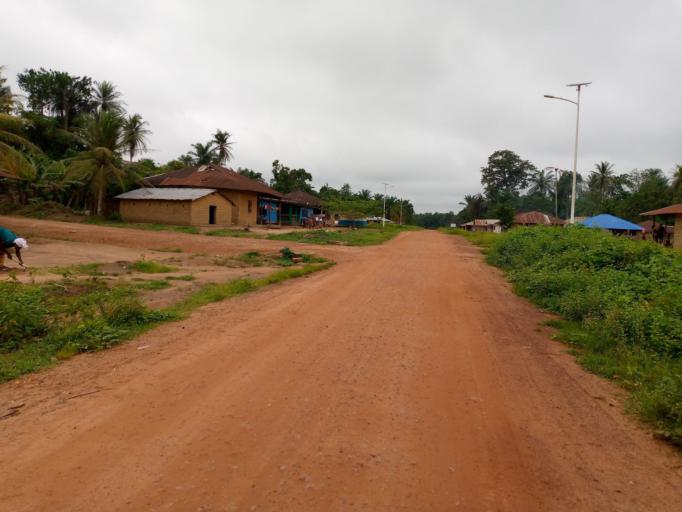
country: SL
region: Southern Province
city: Sumbuya
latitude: 7.5959
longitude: -12.0845
